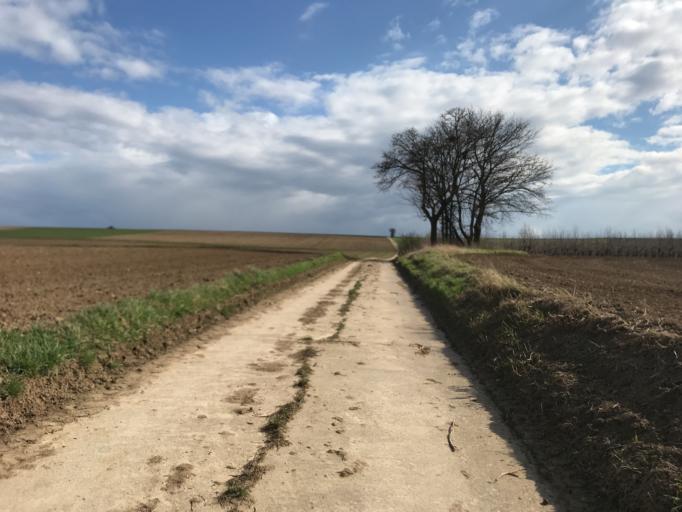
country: DE
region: Rheinland-Pfalz
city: Essenheim
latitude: 49.9083
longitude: 8.1709
